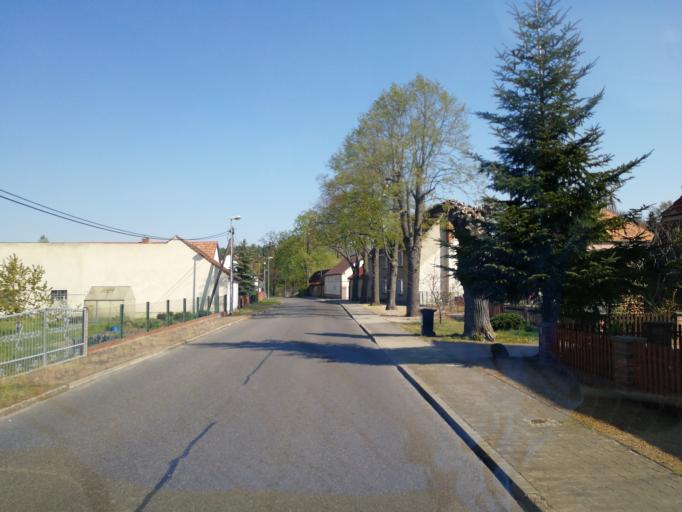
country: DE
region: Brandenburg
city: Bronkow
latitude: 51.7222
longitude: 13.8579
